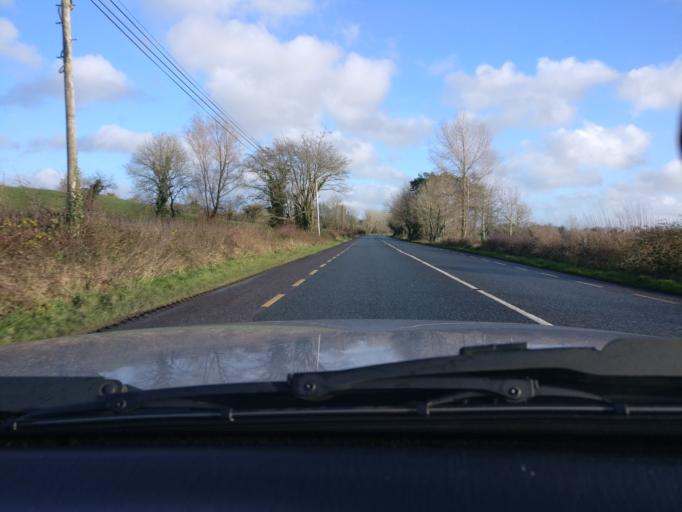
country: IE
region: Leinster
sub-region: Uibh Fhaili
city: Clara
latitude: 53.3983
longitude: -7.6030
